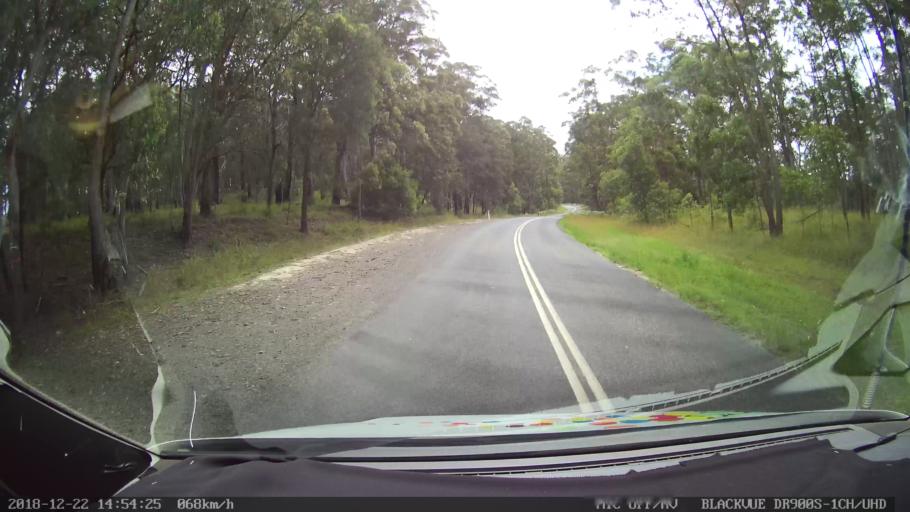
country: AU
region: New South Wales
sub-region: Bellingen
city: Dorrigo
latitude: -30.2263
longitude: 152.5329
